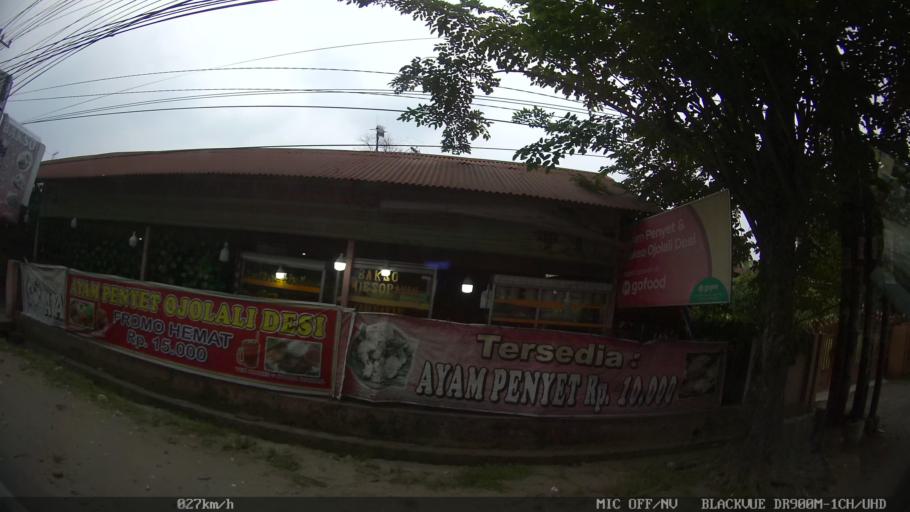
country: ID
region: North Sumatra
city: Medan
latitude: 3.5685
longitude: 98.7106
